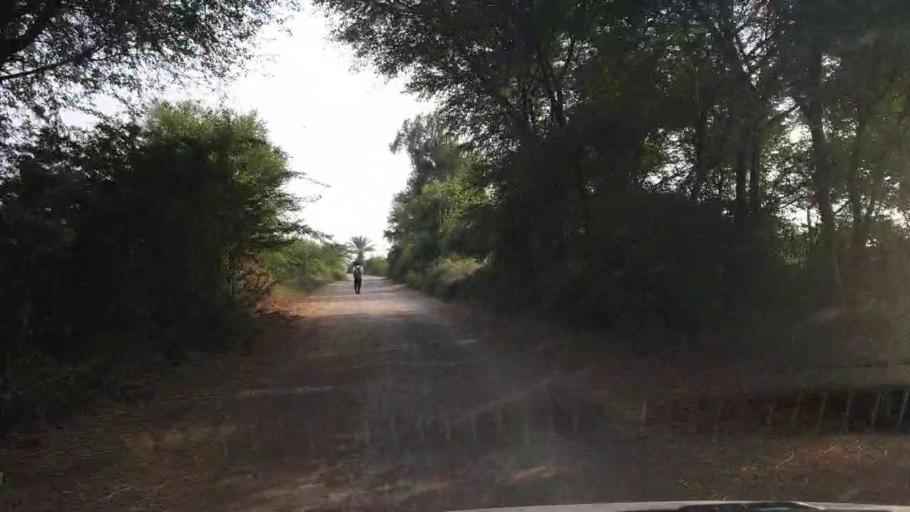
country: PK
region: Sindh
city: Matli
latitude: 25.0633
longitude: 68.7603
